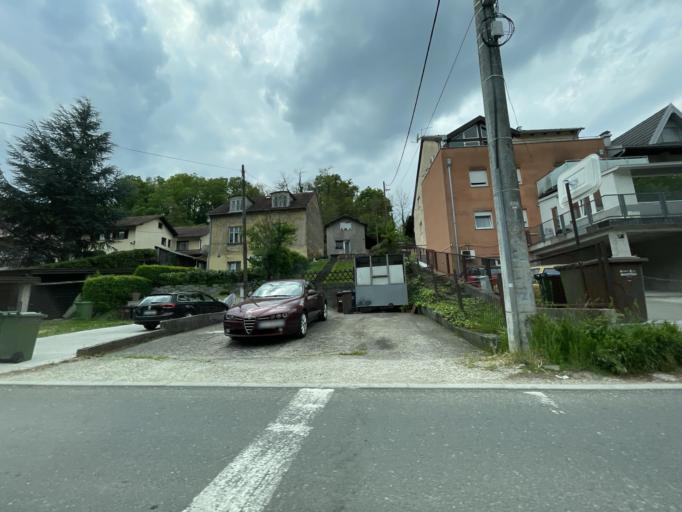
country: HR
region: Grad Zagreb
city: Zagreb - Centar
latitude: 45.8224
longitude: 15.9439
